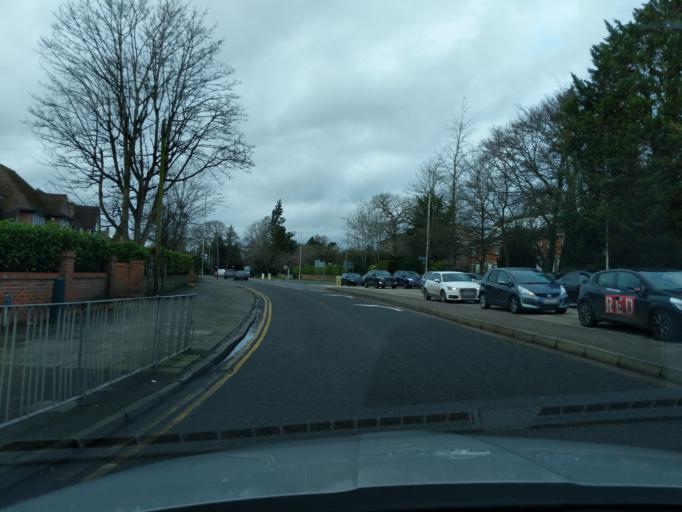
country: GB
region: England
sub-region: Hertfordshire
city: Watford
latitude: 51.6695
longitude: -0.4133
